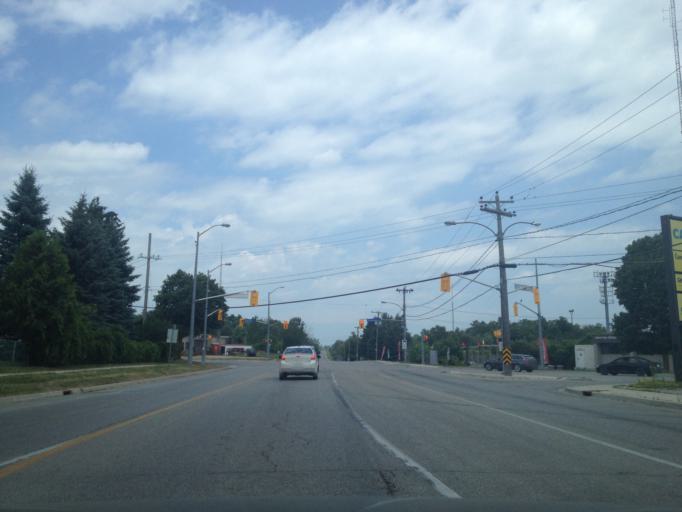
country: CA
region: Ontario
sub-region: Wellington County
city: Guelph
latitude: 43.5741
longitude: -80.2476
